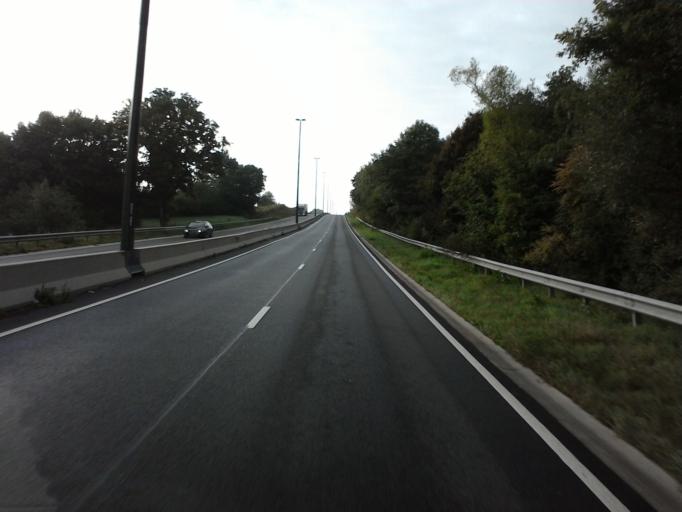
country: BE
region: Wallonia
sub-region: Province du Luxembourg
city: Attert
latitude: 49.7470
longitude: 5.7823
